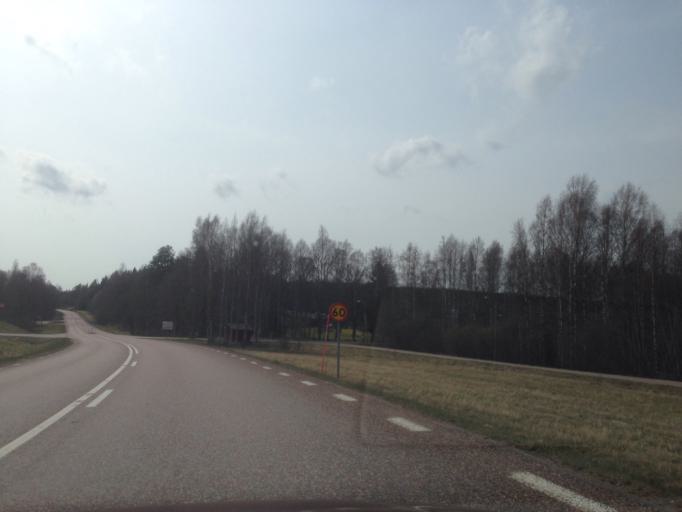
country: SE
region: Dalarna
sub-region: Ludvika Kommun
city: Grangesberg
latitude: 60.2180
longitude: 14.9571
